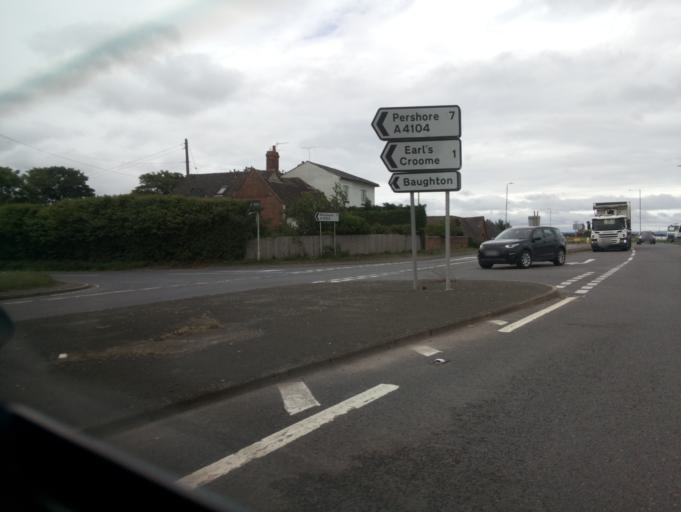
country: GB
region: England
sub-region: Worcestershire
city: Upton upon Severn
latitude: 52.0714
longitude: -2.1990
